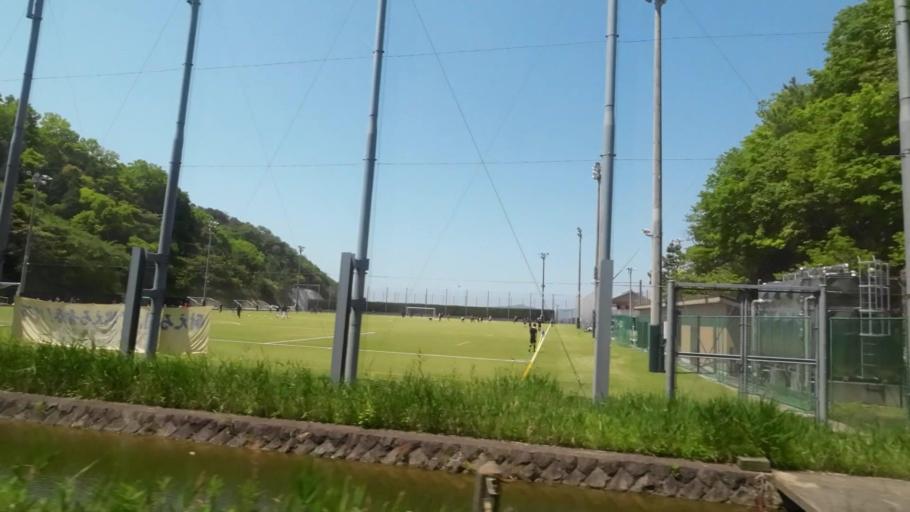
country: JP
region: Ehime
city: Hojo
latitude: 33.9961
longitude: 132.7754
